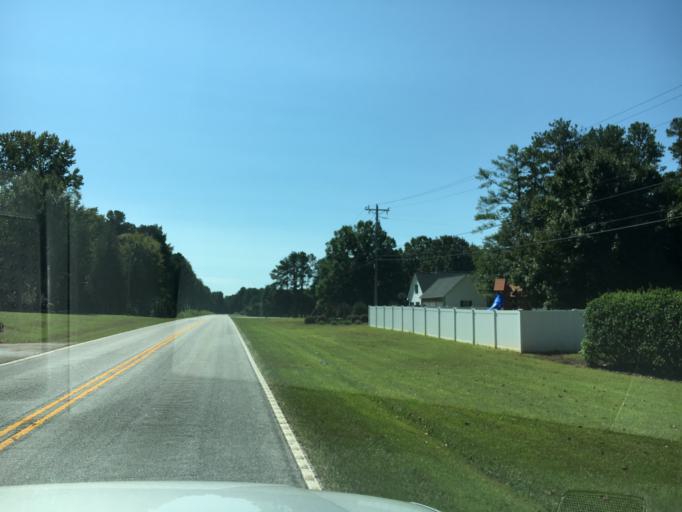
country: US
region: South Carolina
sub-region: Laurens County
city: Clinton
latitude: 34.4400
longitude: -81.8694
